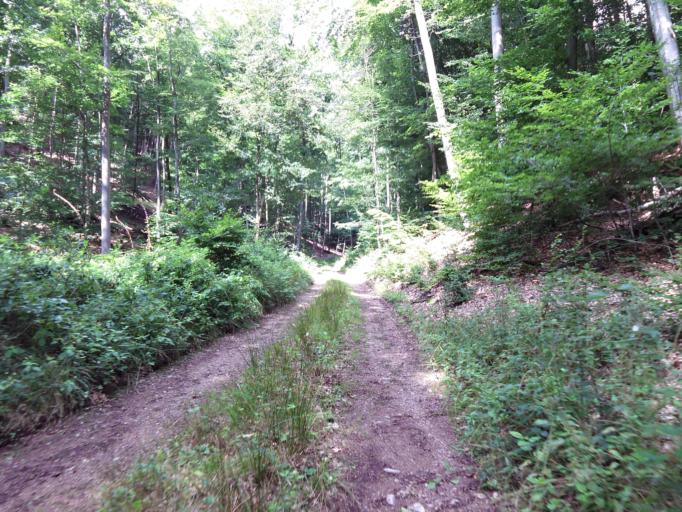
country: DE
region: Rheinland-Pfalz
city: Steinbach am Donnersberg
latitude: 49.5991
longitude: 7.9198
